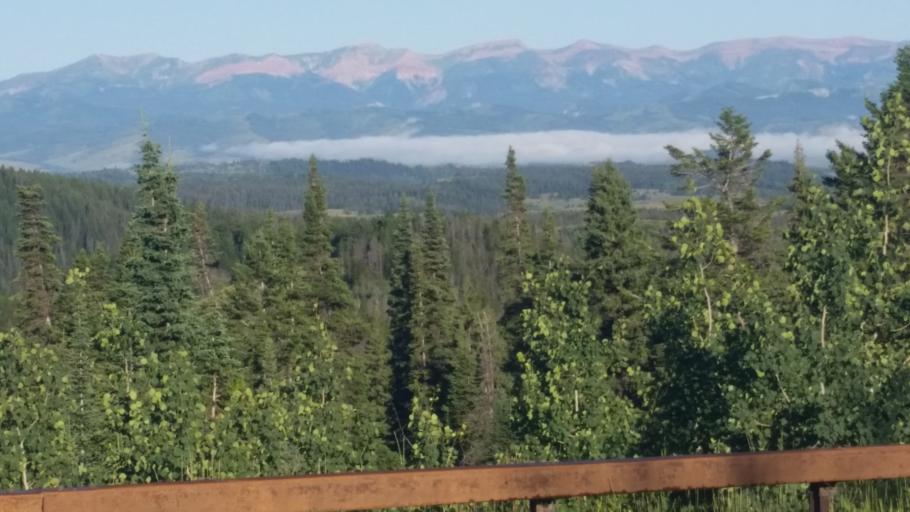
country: US
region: Wyoming
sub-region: Sublette County
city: Pinedale
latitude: 43.1348
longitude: -110.2067
